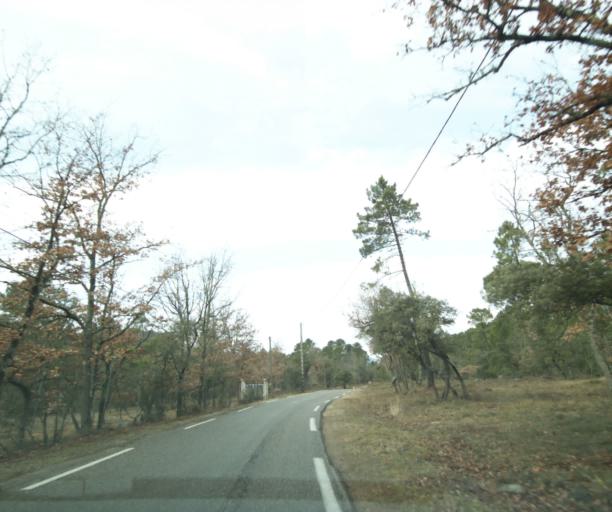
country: FR
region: Provence-Alpes-Cote d'Azur
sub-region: Departement du Var
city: Tourves
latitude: 43.3831
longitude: 5.8941
